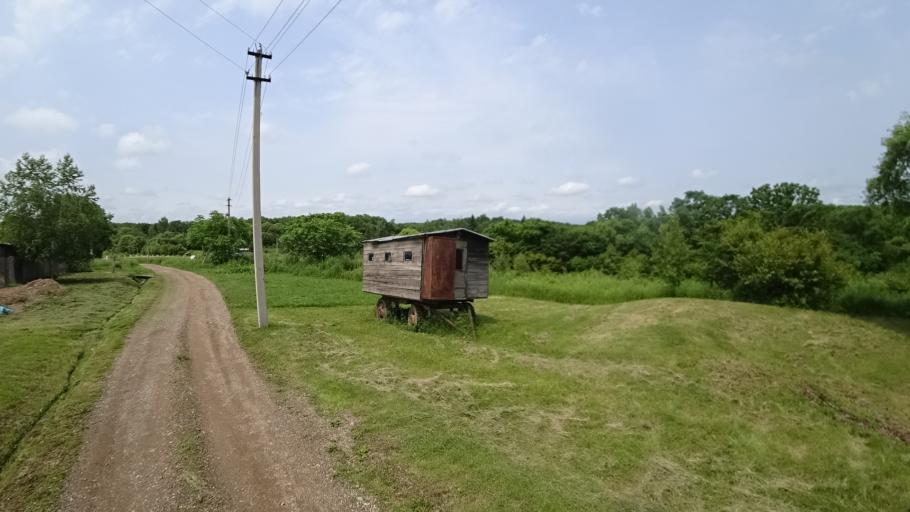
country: RU
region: Primorskiy
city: Novosysoyevka
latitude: 44.2538
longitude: 133.3763
